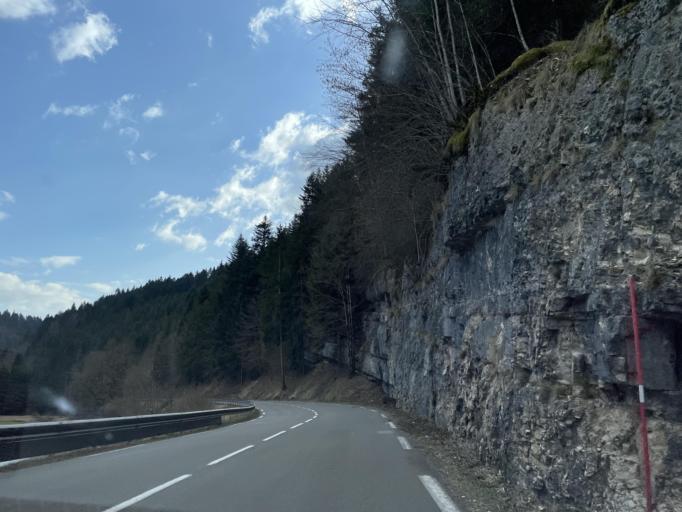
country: FR
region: Franche-Comte
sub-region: Departement du Doubs
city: Gilley
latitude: 47.0252
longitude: 6.4931
